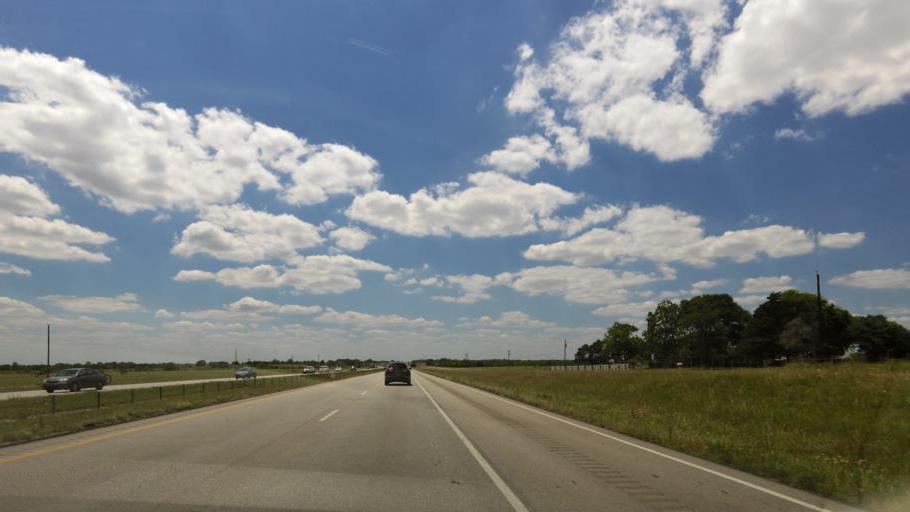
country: US
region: Texas
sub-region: Colorado County
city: Eagle Lake
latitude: 29.7317
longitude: -96.3792
